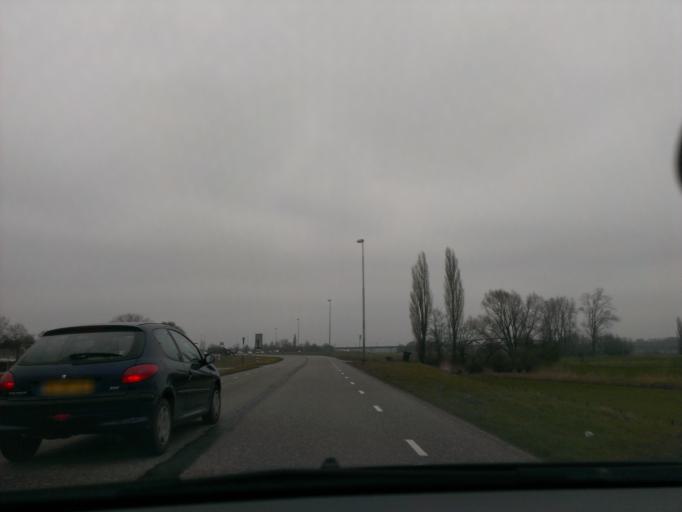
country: NL
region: Gelderland
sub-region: Gemeente Hattem
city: Hattem
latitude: 52.4794
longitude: 6.0641
